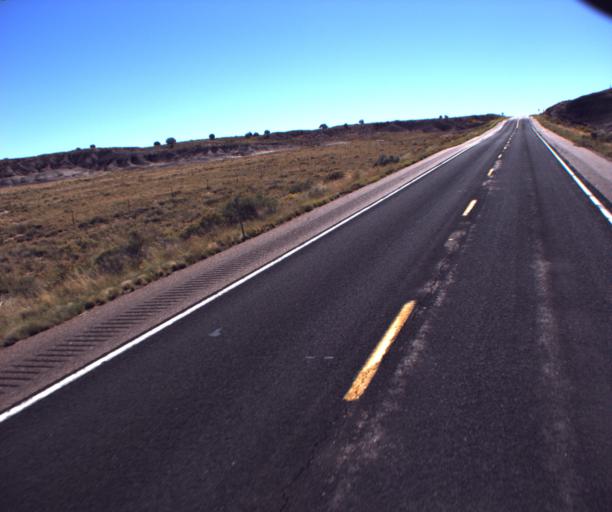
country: US
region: Arizona
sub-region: Navajo County
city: Snowflake
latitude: 34.7191
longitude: -109.7712
